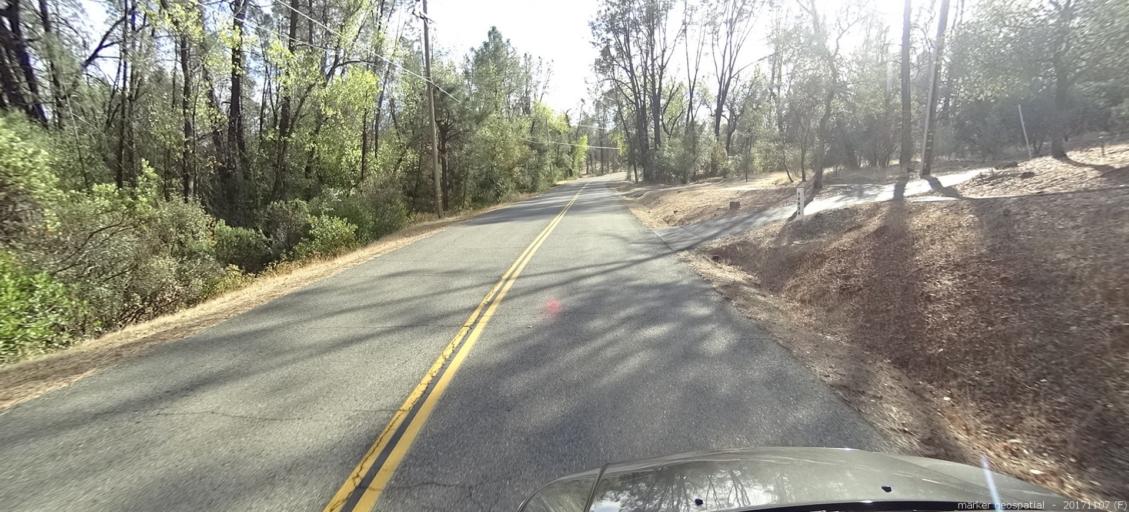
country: US
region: California
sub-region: Shasta County
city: Redding
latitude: 40.5135
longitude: -122.4402
